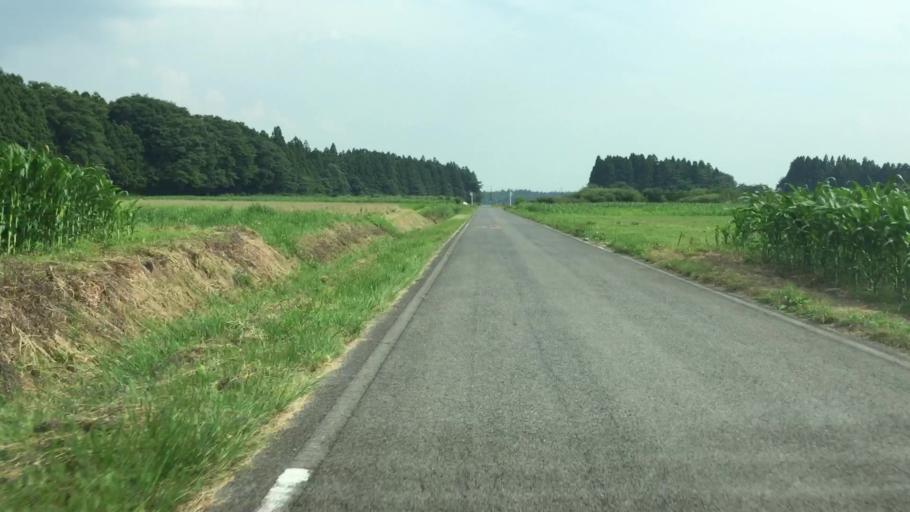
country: JP
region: Tochigi
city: Kuroiso
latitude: 37.0156
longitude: 139.9496
